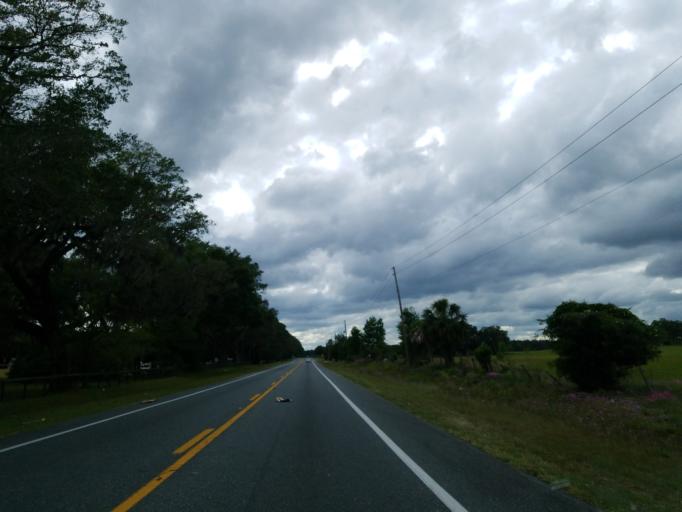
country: US
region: Florida
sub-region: Marion County
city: Ocala
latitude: 29.2595
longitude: -82.0995
